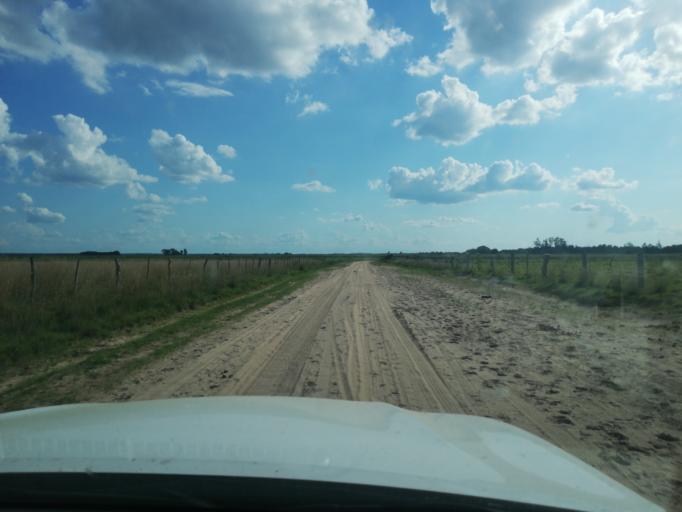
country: AR
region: Corrientes
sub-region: Departamento de San Miguel
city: San Miguel
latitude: -27.9936
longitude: -57.5722
